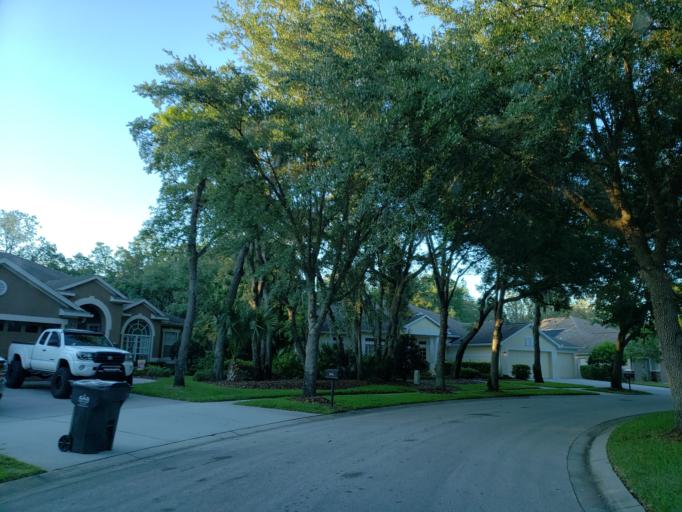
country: US
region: Florida
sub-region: Hillsborough County
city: Fish Hawk
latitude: 27.8364
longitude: -82.2201
